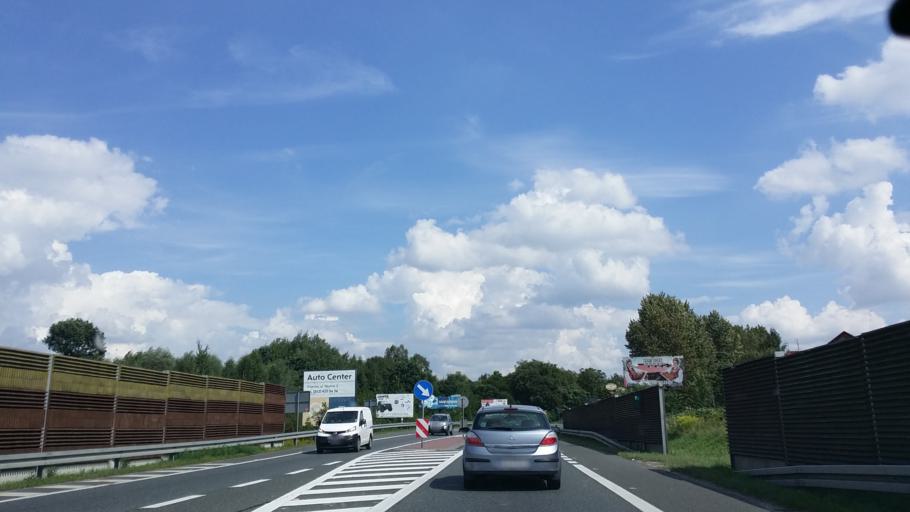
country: PL
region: Lesser Poland Voivodeship
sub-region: Powiat wielicki
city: Wieliczka
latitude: 49.9940
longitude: 20.0754
